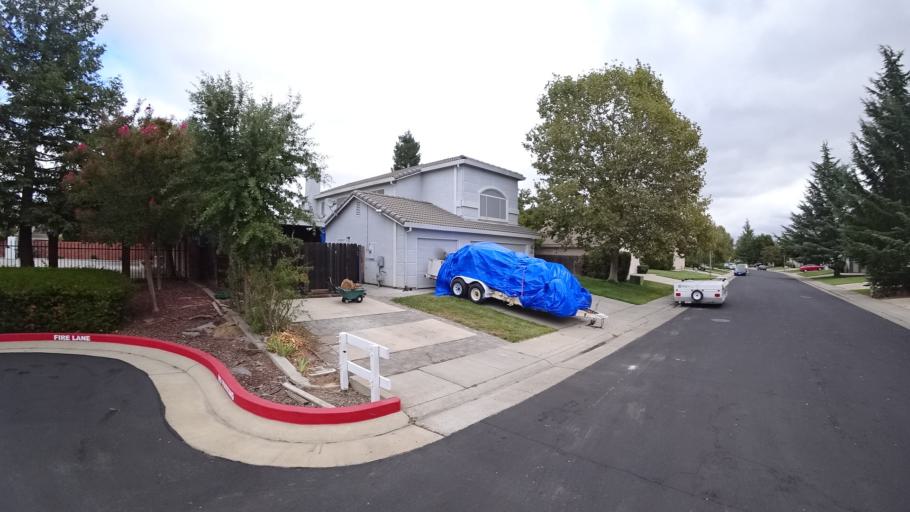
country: US
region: California
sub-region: Sacramento County
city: Laguna
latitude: 38.4108
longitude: -121.4292
